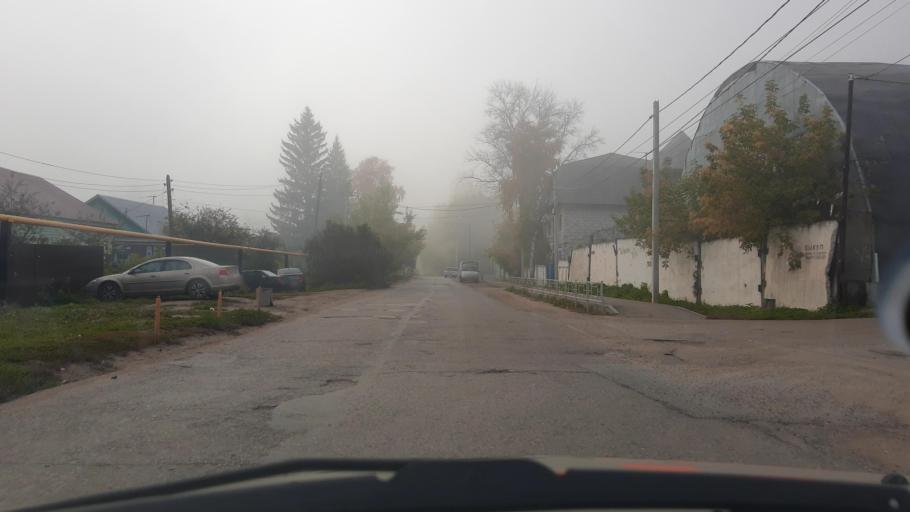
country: RU
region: Bashkortostan
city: Mikhaylovka
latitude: 54.6932
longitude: 55.8493
